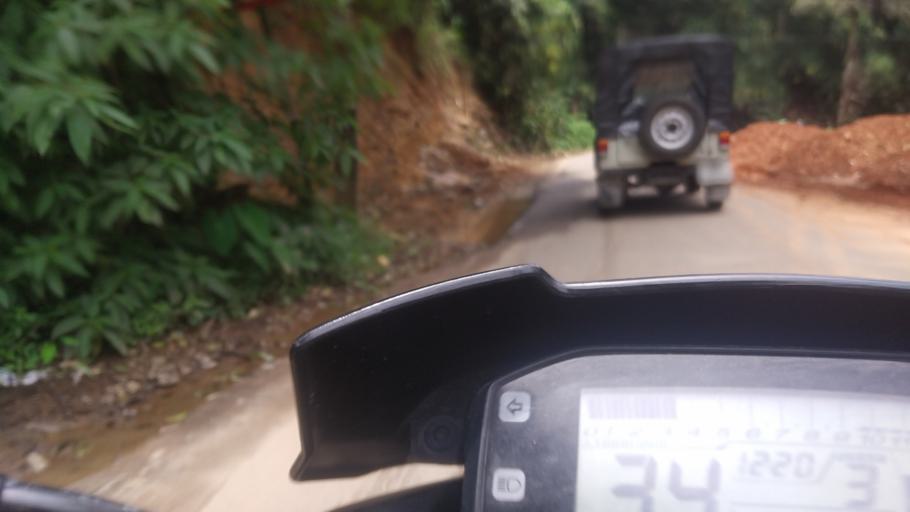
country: IN
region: Kerala
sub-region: Idukki
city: Munnar
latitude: 10.0232
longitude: 76.9987
